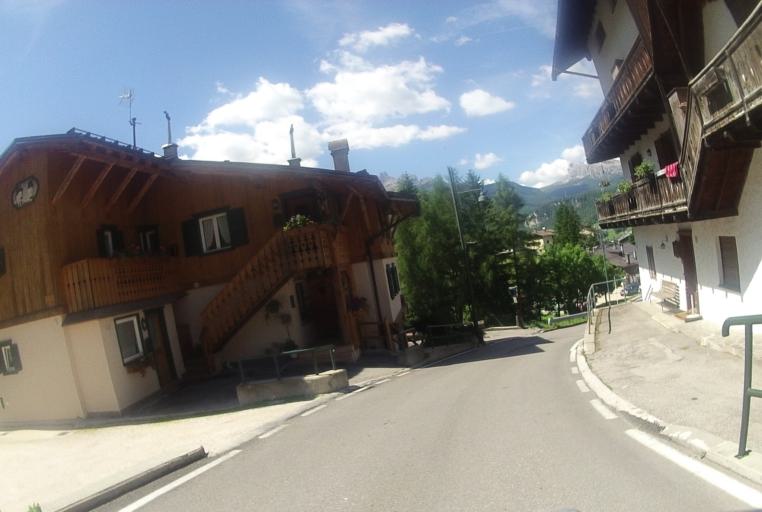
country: IT
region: Veneto
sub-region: Provincia di Belluno
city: Cortina d'Ampezzo
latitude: 46.5442
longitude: 12.1531
